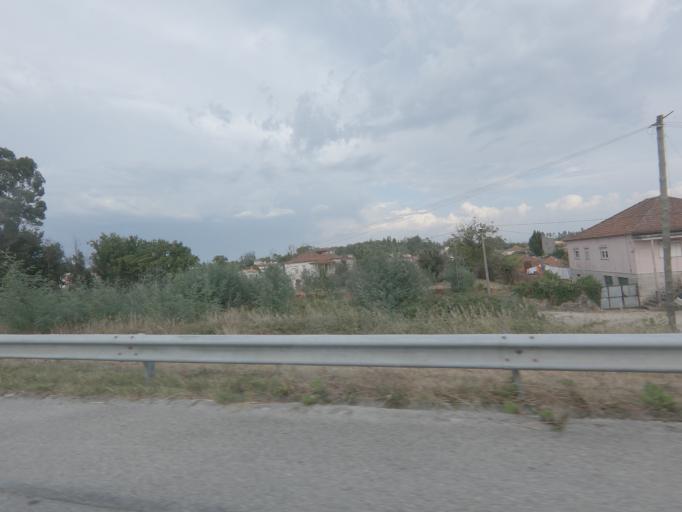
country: PT
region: Viseu
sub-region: Santa Comba Dao
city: Santa Comba Dao
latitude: 40.4182
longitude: -8.1222
